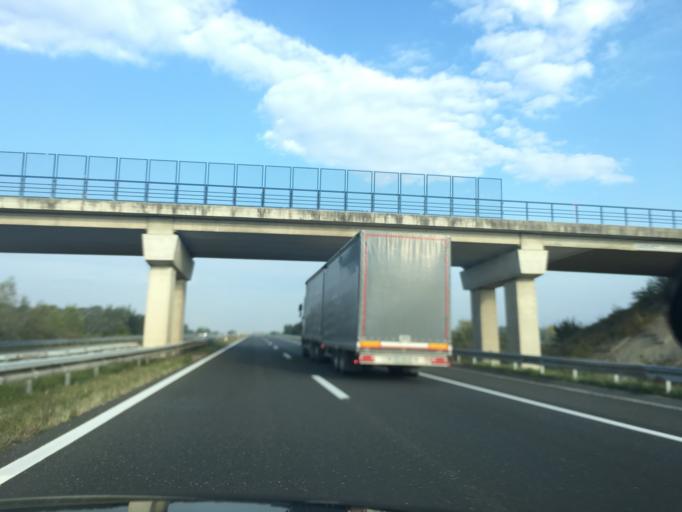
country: HR
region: Zagrebacka
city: Bestovje
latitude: 45.8071
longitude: 15.7719
